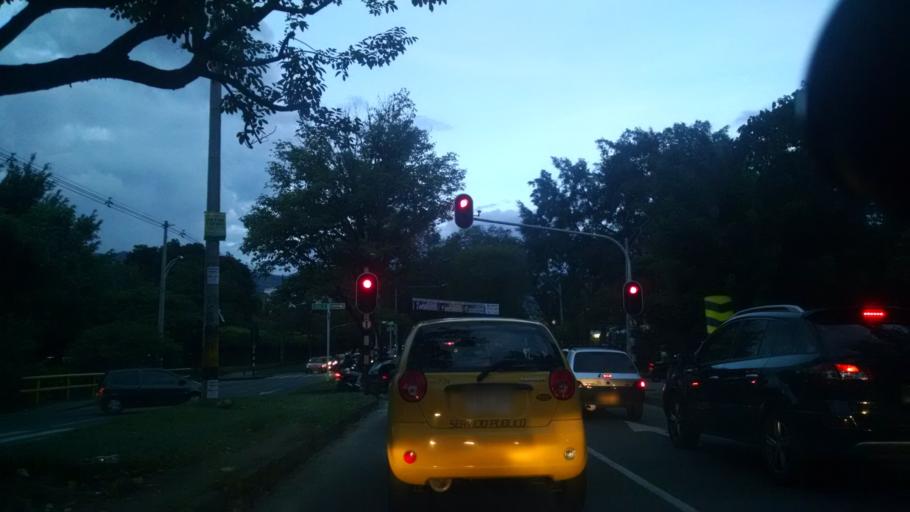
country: CO
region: Antioquia
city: Itagui
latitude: 6.2164
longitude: -75.5979
